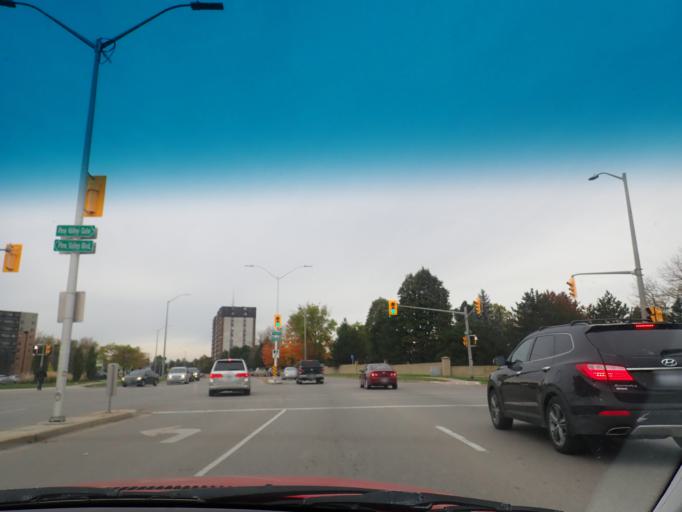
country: CA
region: Ontario
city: London
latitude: 42.9420
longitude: -81.2826
